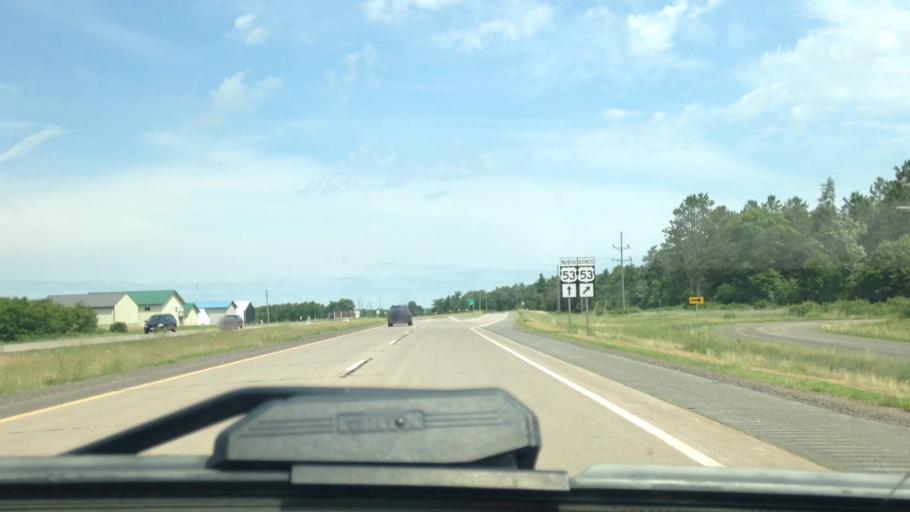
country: US
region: Wisconsin
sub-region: Douglas County
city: Lake Nebagamon
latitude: 46.3158
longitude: -91.8119
